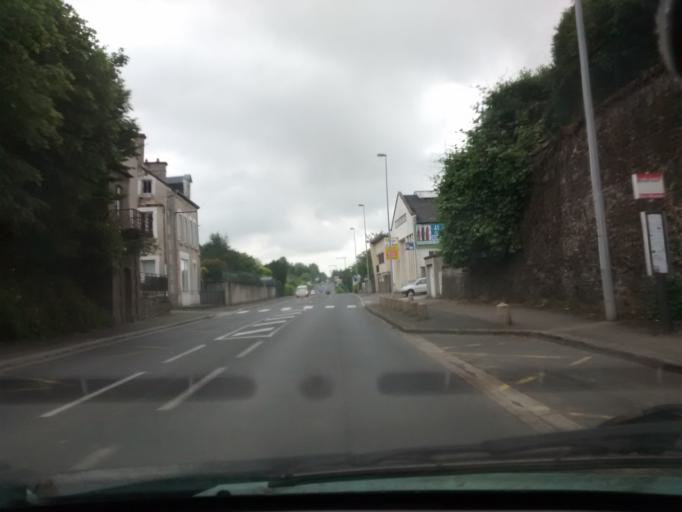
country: FR
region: Lower Normandy
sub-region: Departement de la Manche
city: Agneaux
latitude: 49.1104
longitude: -1.1037
